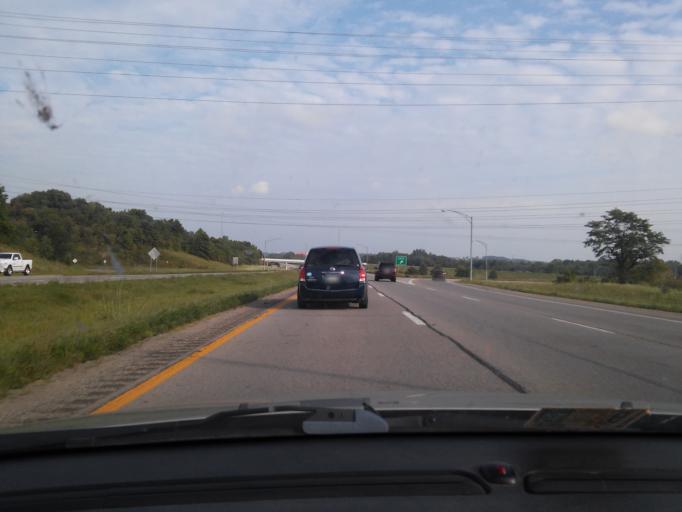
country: US
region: Ohio
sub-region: Jackson County
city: Jackson
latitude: 39.0490
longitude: -82.6166
